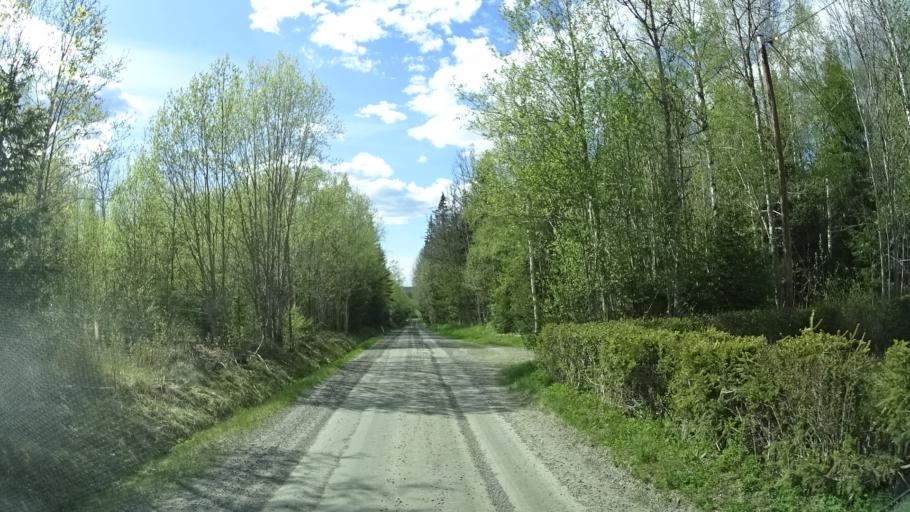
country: SE
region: OErebro
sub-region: Nora Kommun
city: As
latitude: 59.4408
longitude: 14.8444
